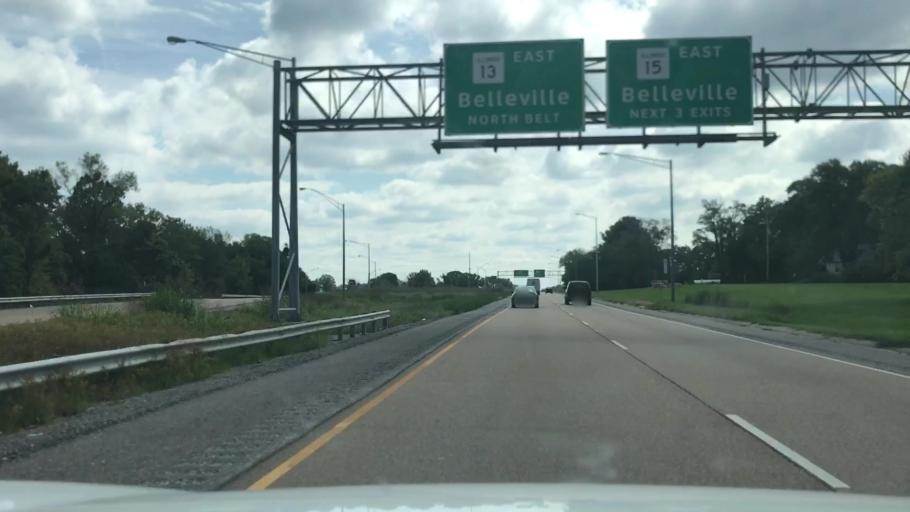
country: US
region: Illinois
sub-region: Saint Clair County
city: Alorton
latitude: 38.5508
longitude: -90.0712
